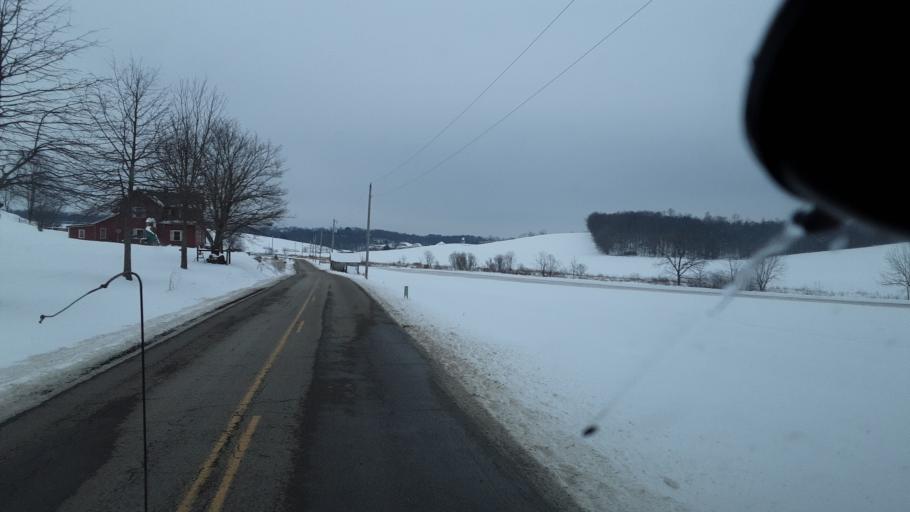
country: US
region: Ohio
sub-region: Perry County
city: Somerset
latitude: 39.8991
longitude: -82.2099
